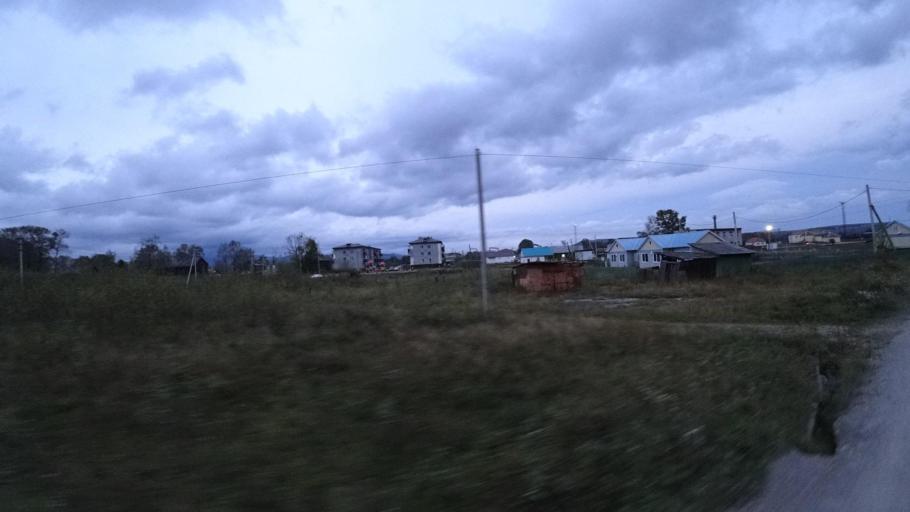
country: RU
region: Jewish Autonomous Oblast
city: Izvestkovyy
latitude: 48.9832
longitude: 131.5498
